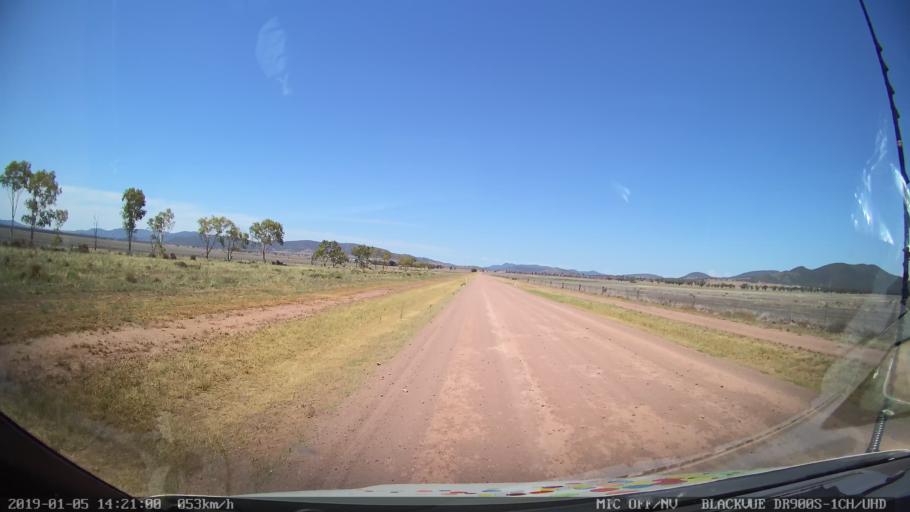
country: AU
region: New South Wales
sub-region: Liverpool Plains
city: Quirindi
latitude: -31.2476
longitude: 150.5096
